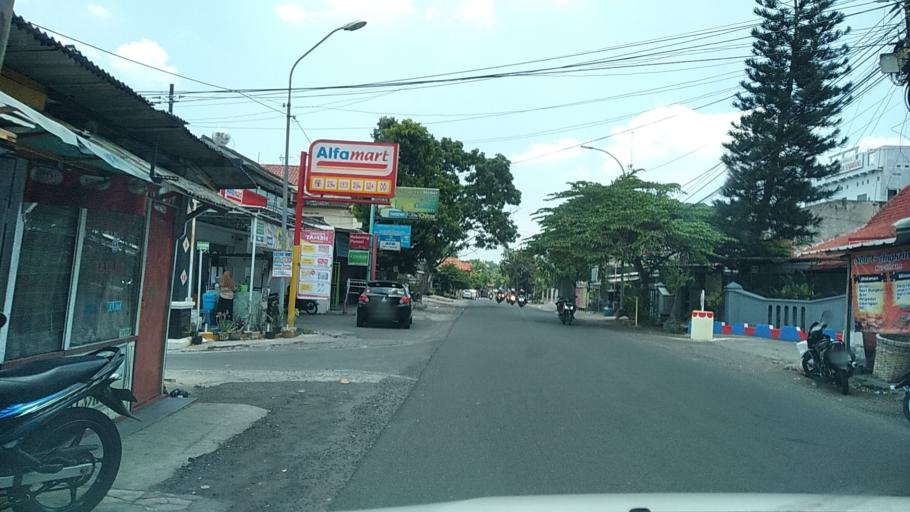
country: ID
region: Central Java
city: Semarang
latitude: -7.0151
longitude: 110.3943
